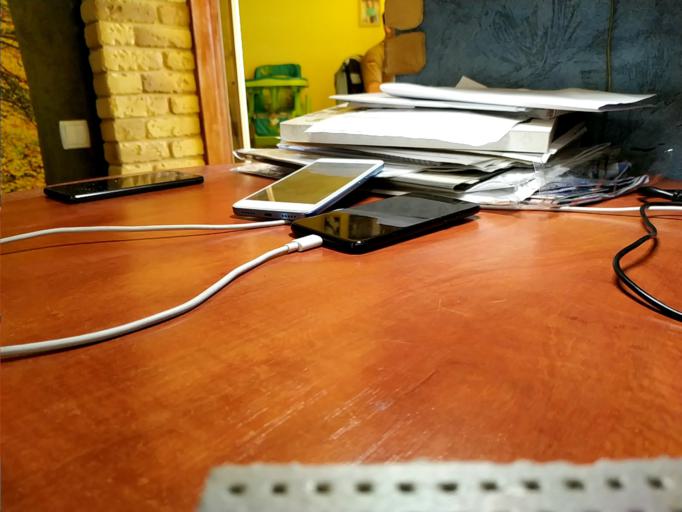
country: RU
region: Tverskaya
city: Spirovo
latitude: 57.4520
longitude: 35.0480
